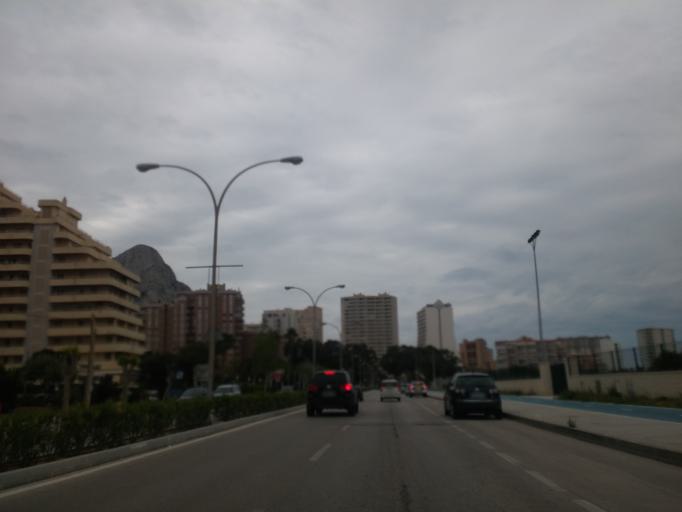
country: ES
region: Valencia
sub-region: Provincia de Alicante
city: Calp
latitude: 38.6466
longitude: 0.0714
